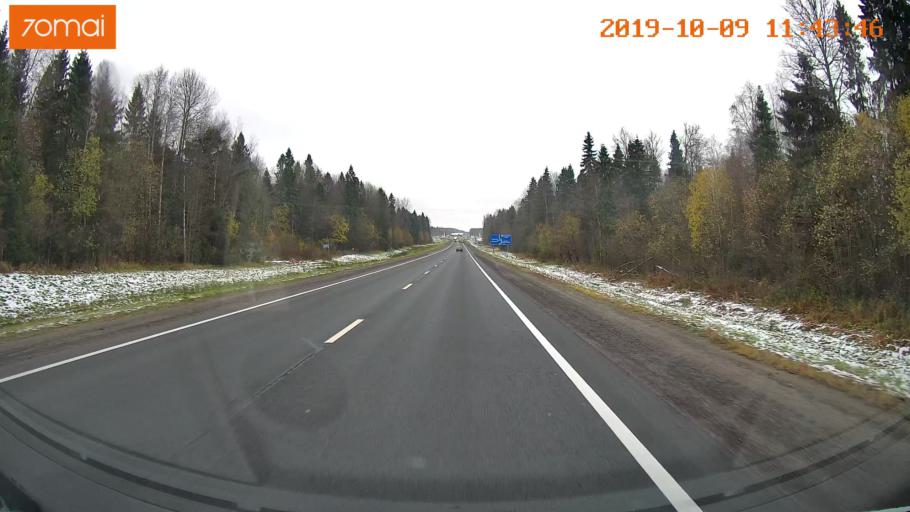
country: RU
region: Vologda
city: Gryazovets
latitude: 58.8923
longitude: 40.1876
